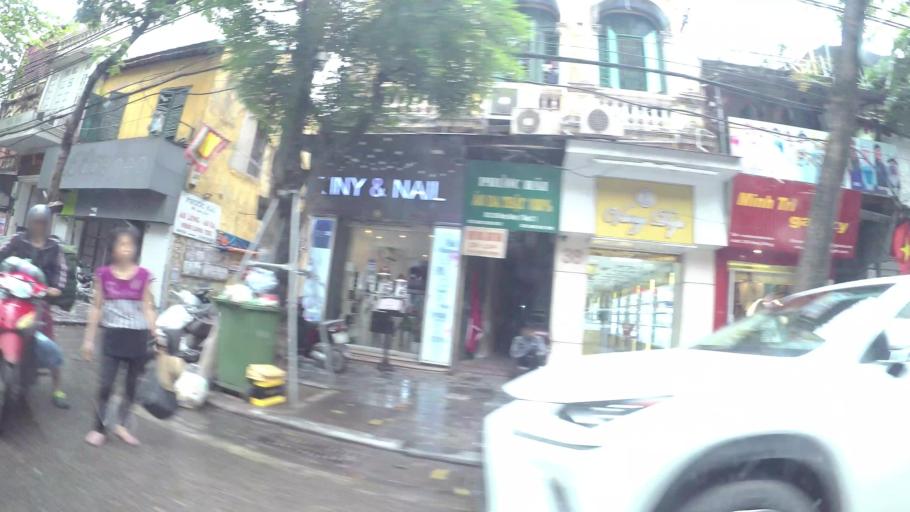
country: VN
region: Ha Noi
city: Hoan Kiem
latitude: 21.0310
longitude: 105.8482
